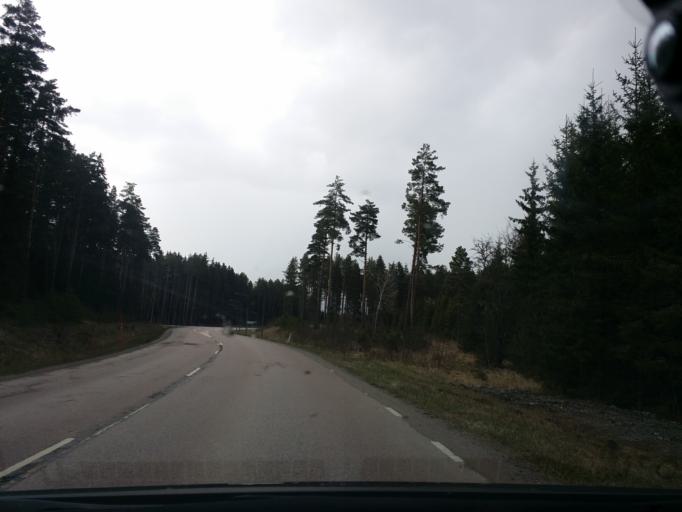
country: SE
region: Uppsala
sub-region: Enkopings Kommun
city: Enkoping
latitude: 59.6244
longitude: 17.1348
